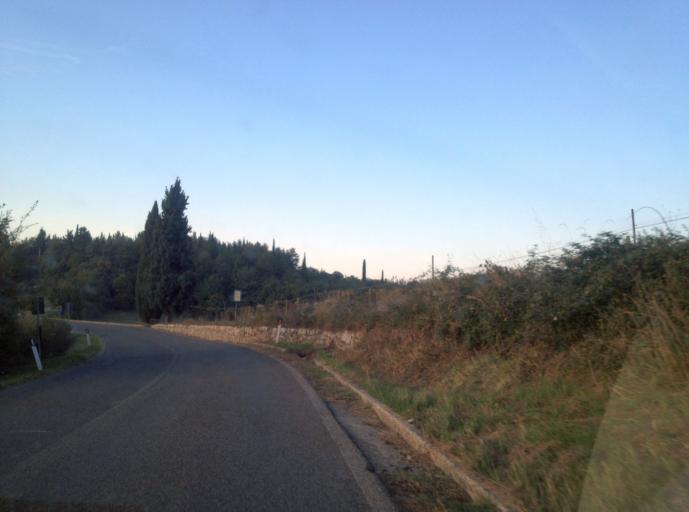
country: IT
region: Tuscany
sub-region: Provincia di Siena
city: Castellina in Chianti
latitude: 43.4489
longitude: 11.2948
